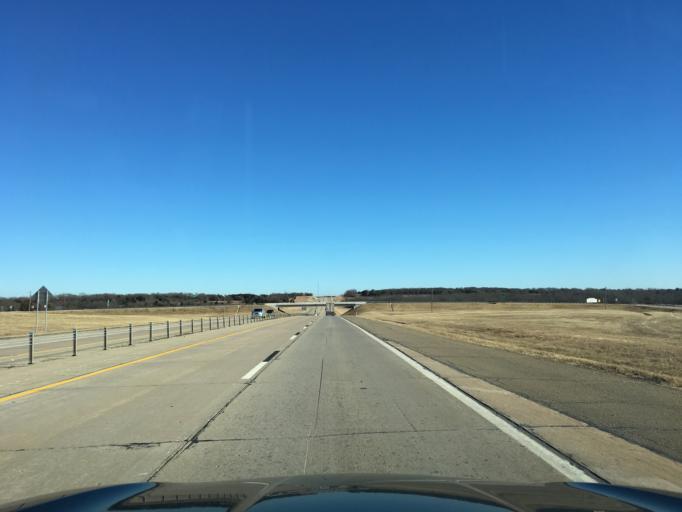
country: US
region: Oklahoma
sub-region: Pawnee County
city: Pawnee
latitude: 36.2248
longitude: -96.7884
